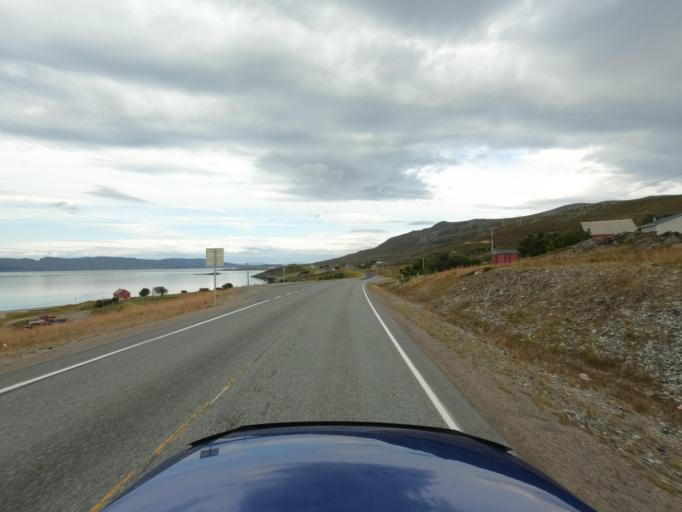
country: NO
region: Finnmark Fylke
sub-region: Hammerfest
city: Rypefjord
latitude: 70.5402
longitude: 23.7366
